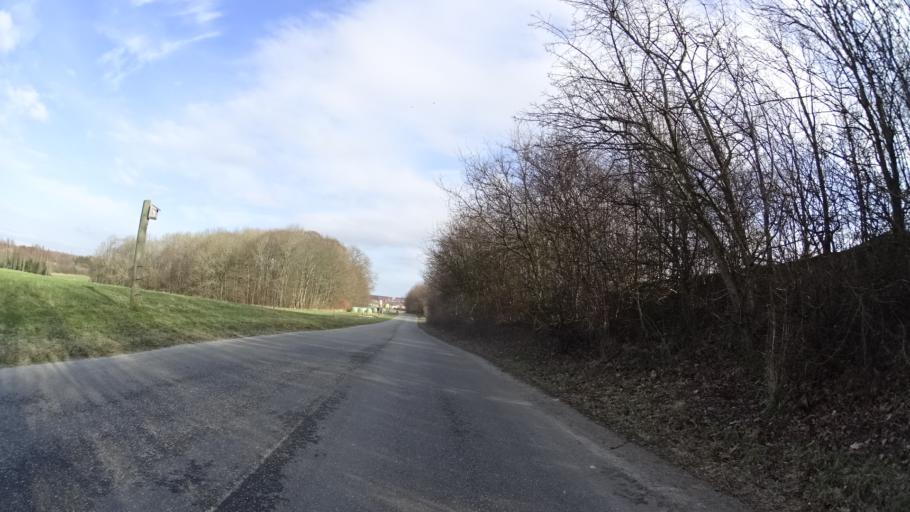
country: DK
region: Central Jutland
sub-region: Arhus Kommune
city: Kolt
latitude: 56.1130
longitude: 10.0794
